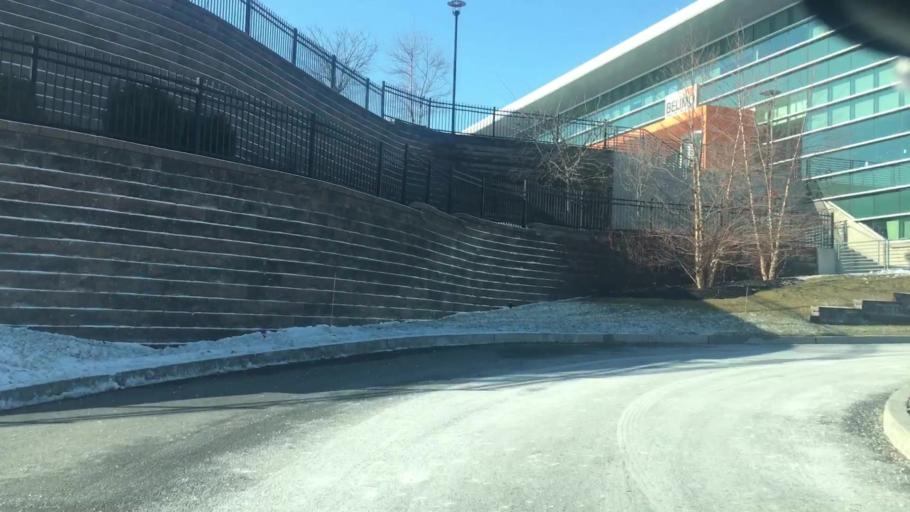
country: US
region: New York
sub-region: Putnam County
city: Peach Lake
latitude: 41.3763
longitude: -73.5404
